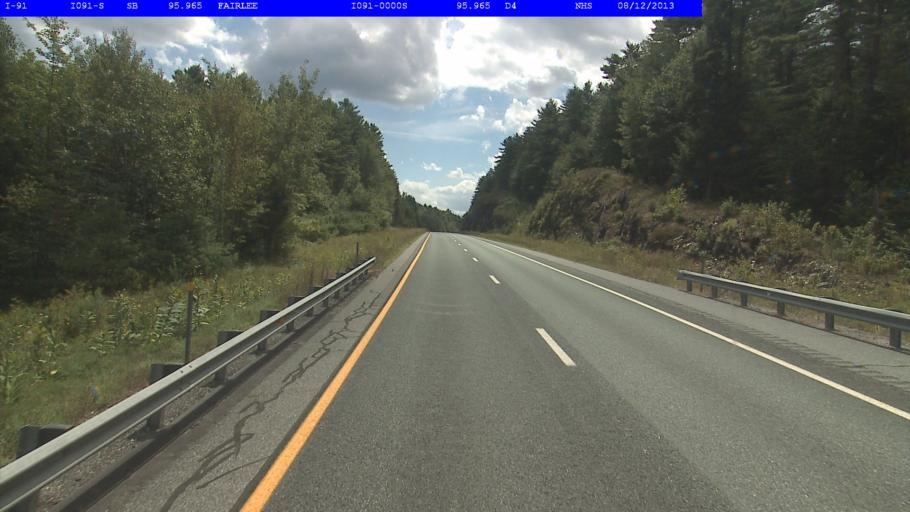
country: US
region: New Hampshire
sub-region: Grafton County
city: Orford
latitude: 43.9612
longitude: -72.1294
